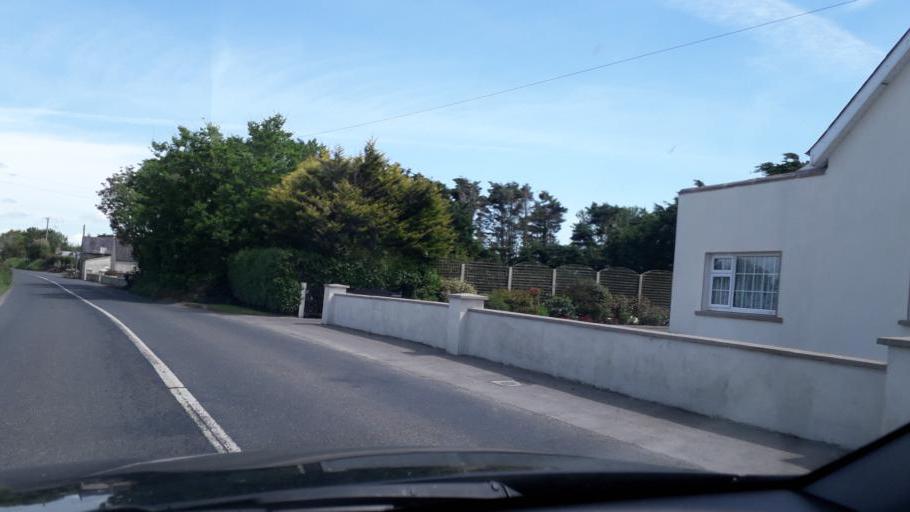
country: IE
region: Leinster
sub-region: Loch Garman
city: Loch Garman
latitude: 52.1911
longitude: -6.5602
